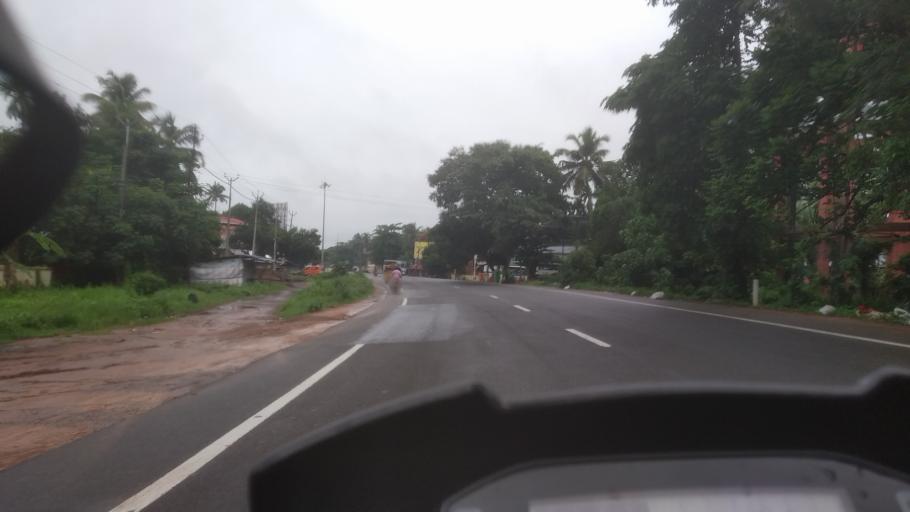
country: IN
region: Kerala
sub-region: Alappuzha
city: Kayankulam
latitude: 9.1605
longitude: 76.5075
